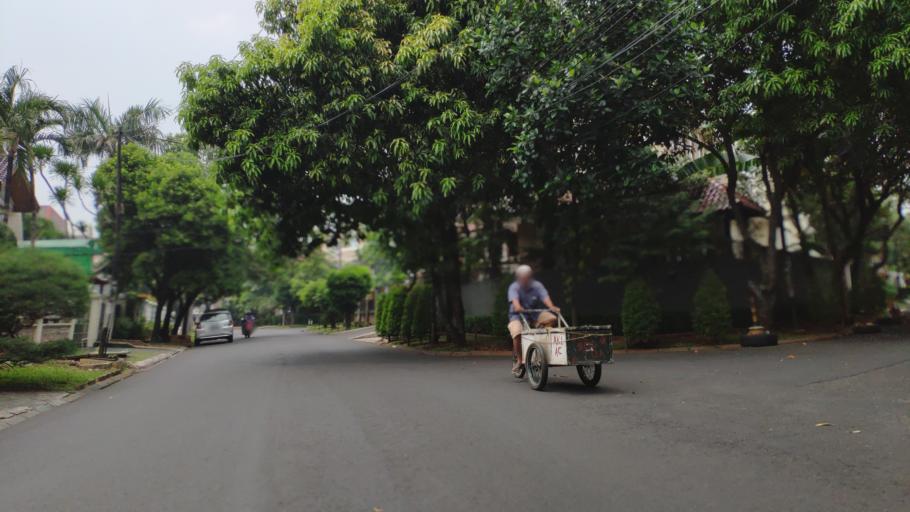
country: ID
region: Banten
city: South Tangerang
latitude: -6.2660
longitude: 106.7792
